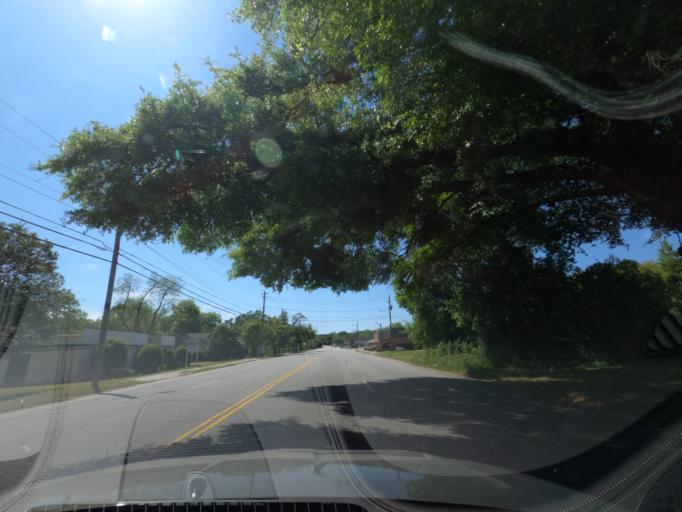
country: US
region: Georgia
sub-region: Richmond County
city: Augusta
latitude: 33.4684
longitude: -81.9991
